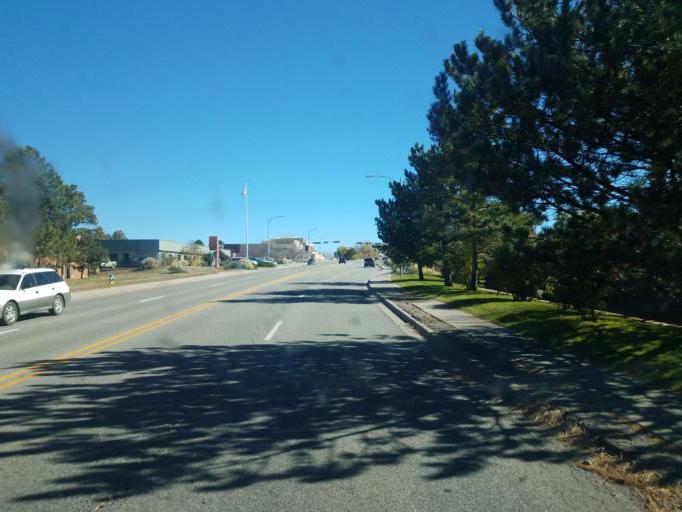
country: US
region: New Mexico
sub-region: Los Alamos County
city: Los Alamos
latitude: 35.8819
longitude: -106.3079
